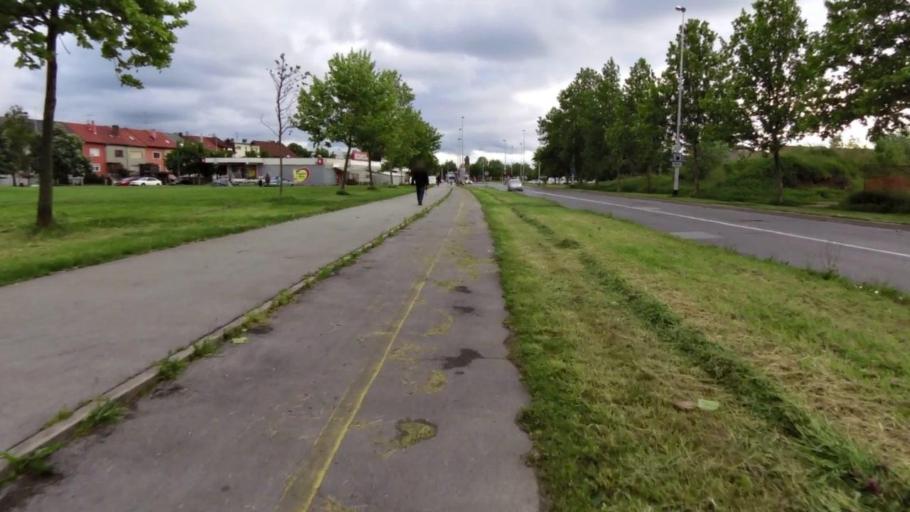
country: HR
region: Grad Zagreb
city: Dubrava
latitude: 45.8390
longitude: 16.0491
